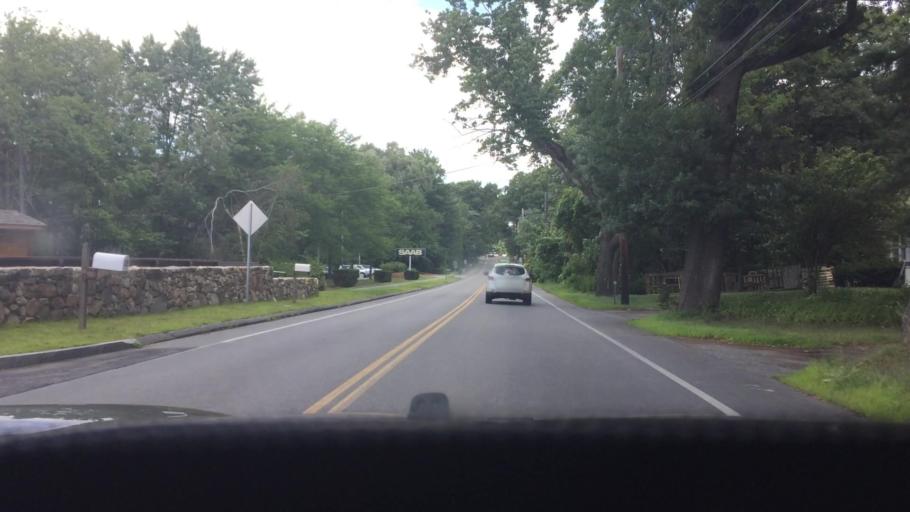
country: US
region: Massachusetts
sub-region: Middlesex County
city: Maynard
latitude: 42.4497
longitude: -71.4542
